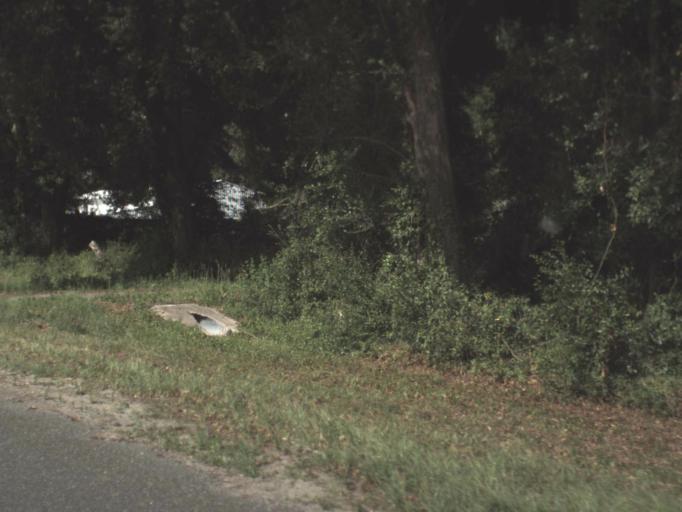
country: US
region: Florida
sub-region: Alachua County
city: High Springs
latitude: 29.9574
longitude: -82.7127
